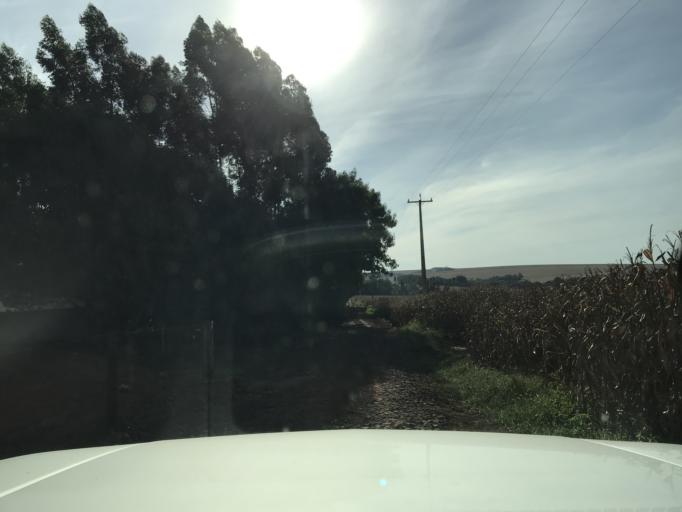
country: BR
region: Parana
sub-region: Palotina
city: Palotina
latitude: -24.2576
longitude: -53.7492
